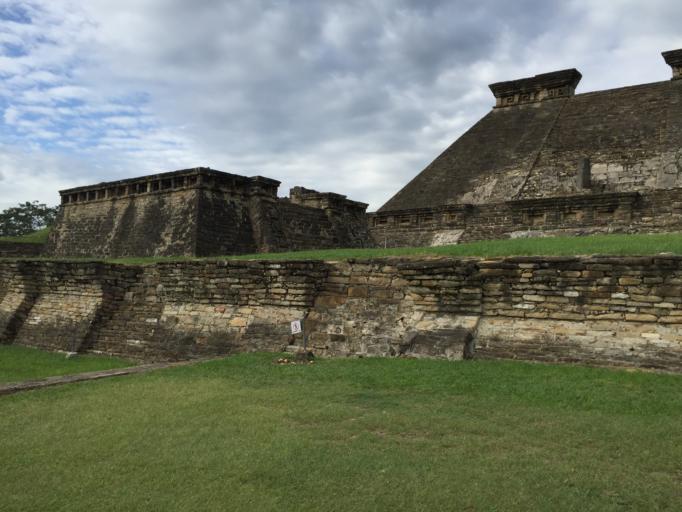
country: MX
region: Veracruz
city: Papantla de Olarte
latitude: 20.4476
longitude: -97.3776
